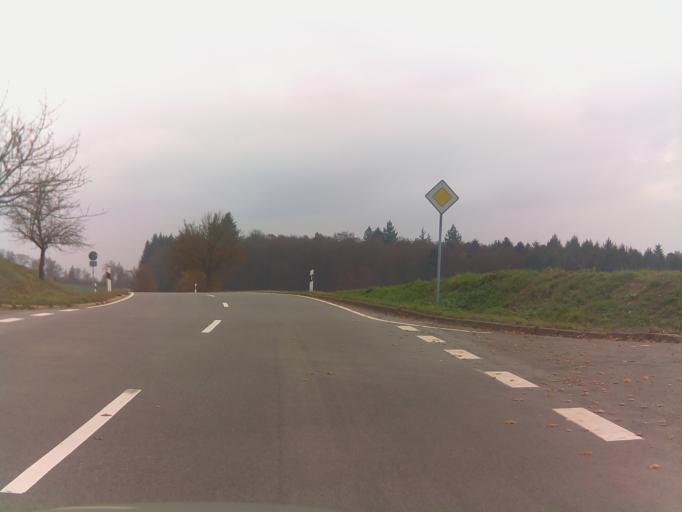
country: DE
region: Baden-Wuerttemberg
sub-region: Karlsruhe Region
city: Neunkirchen
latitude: 49.4015
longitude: 8.9785
